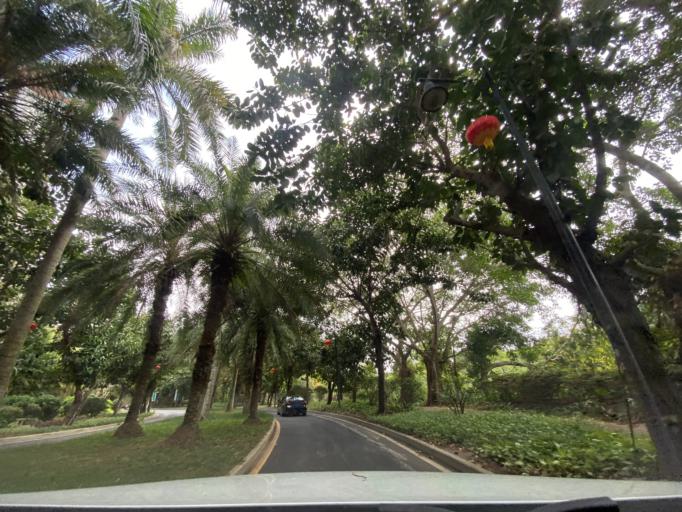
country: CN
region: Hainan
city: Liji
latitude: 18.6689
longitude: 110.2717
